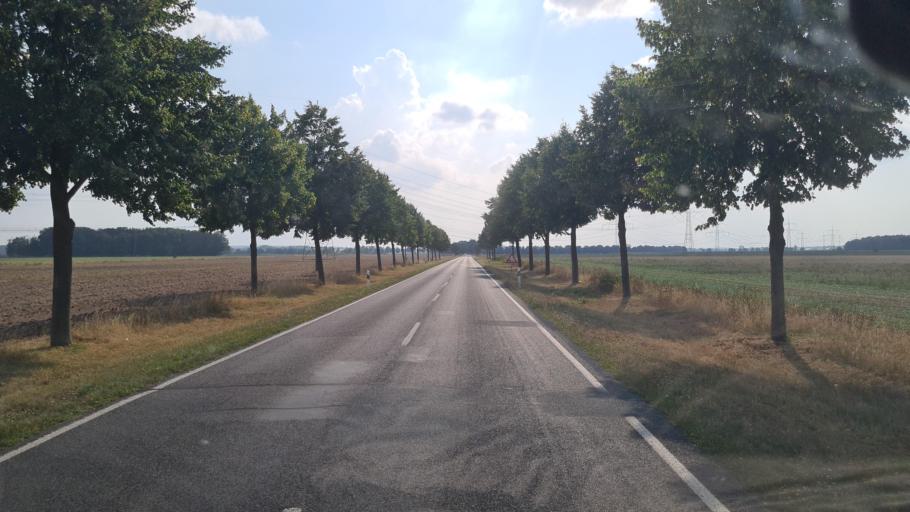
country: DE
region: Brandenburg
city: Dahme
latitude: 51.8470
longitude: 13.3985
